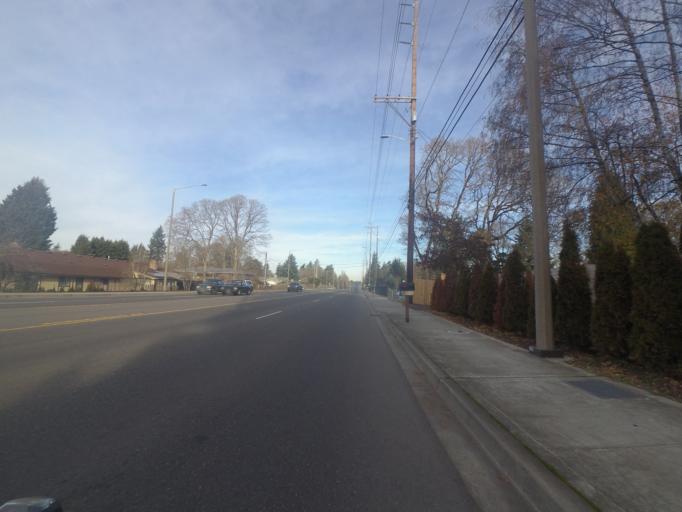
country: US
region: Washington
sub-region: Pierce County
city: Lakewood
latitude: 47.1804
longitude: -122.5180
